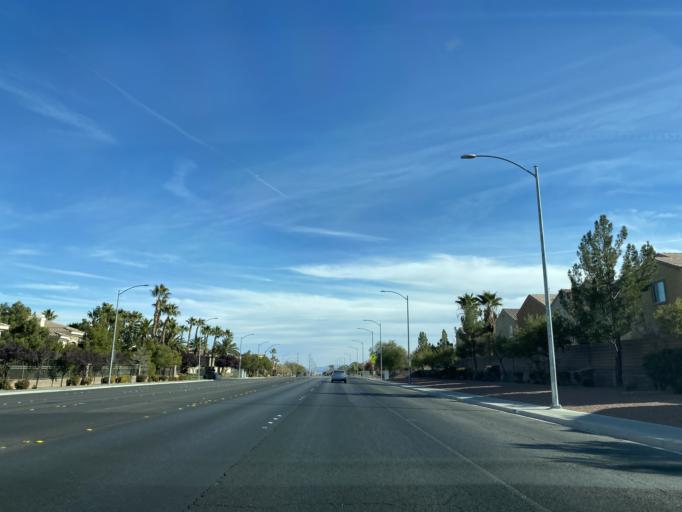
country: US
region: Nevada
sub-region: Clark County
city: Enterprise
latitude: 36.0554
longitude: -115.2906
